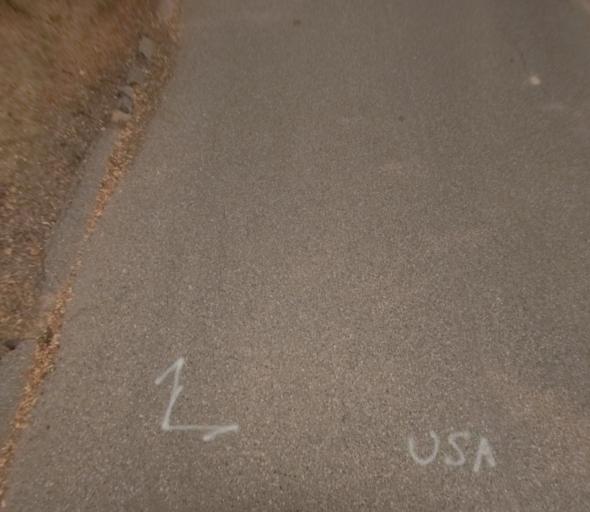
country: US
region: California
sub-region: Madera County
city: Coarsegold
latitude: 37.2238
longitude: -119.7212
